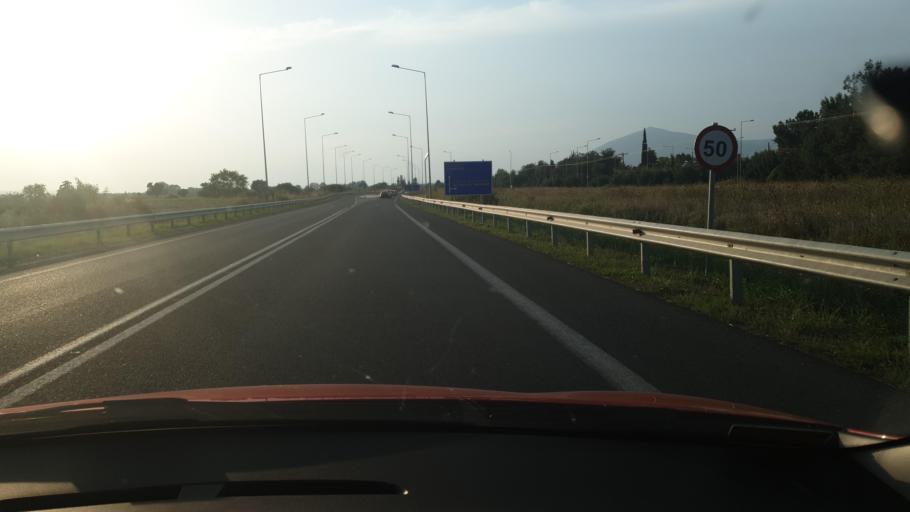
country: GR
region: Central Macedonia
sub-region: Nomos Thessalonikis
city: Vasilika
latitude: 40.4758
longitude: 23.1650
